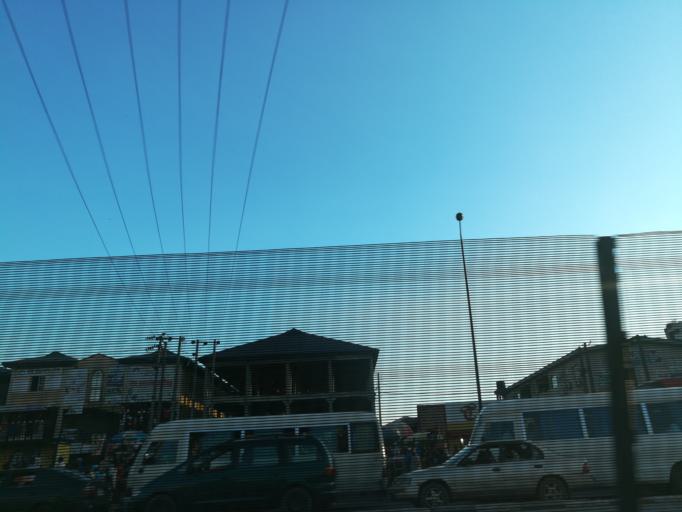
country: NG
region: Lagos
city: Ikorodu
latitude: 6.6224
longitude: 3.4992
